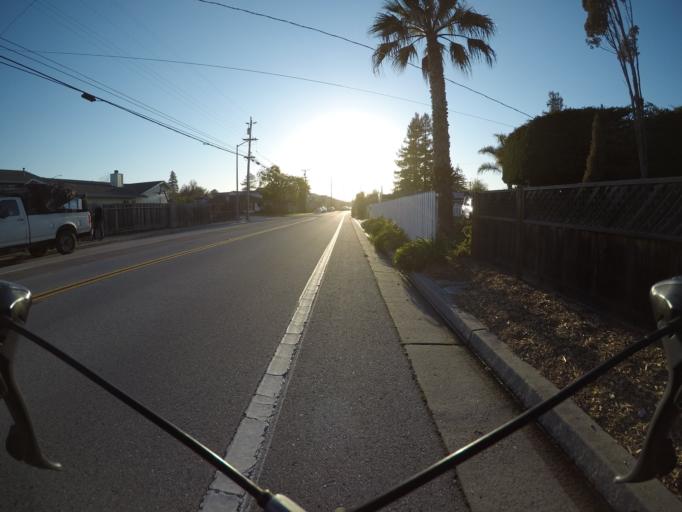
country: US
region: California
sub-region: Santa Cruz County
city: Live Oak
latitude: 36.9818
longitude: -121.9866
